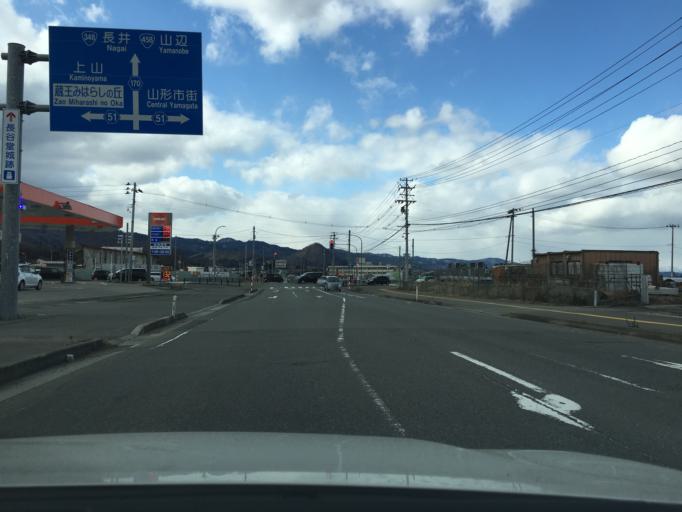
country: JP
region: Yamagata
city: Kaminoyama
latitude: 38.2092
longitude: 140.3010
